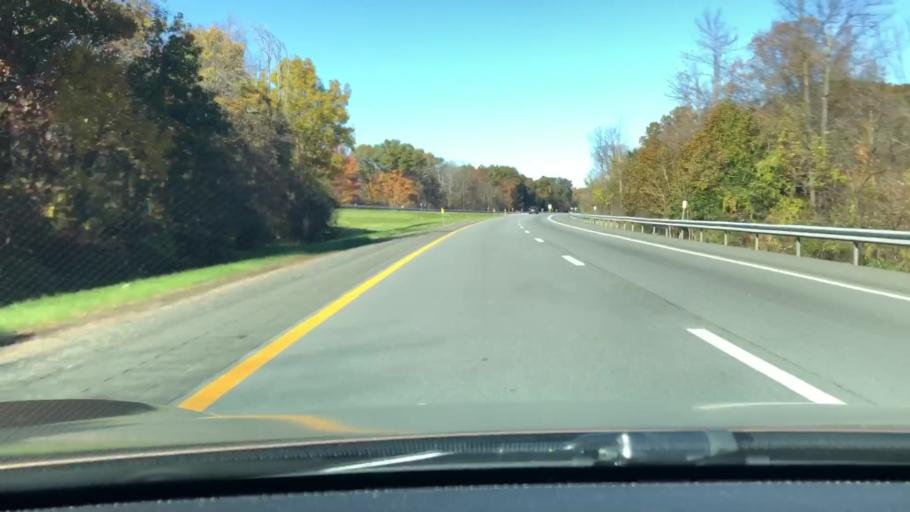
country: US
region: New York
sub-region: Orange County
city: Vails Gate
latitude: 41.4802
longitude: -74.0783
